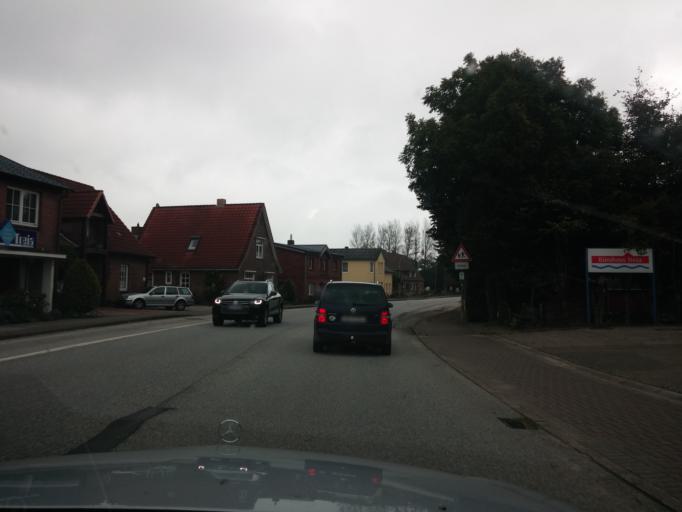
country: DE
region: Schleswig-Holstein
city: Treia
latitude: 54.5143
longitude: 9.3139
